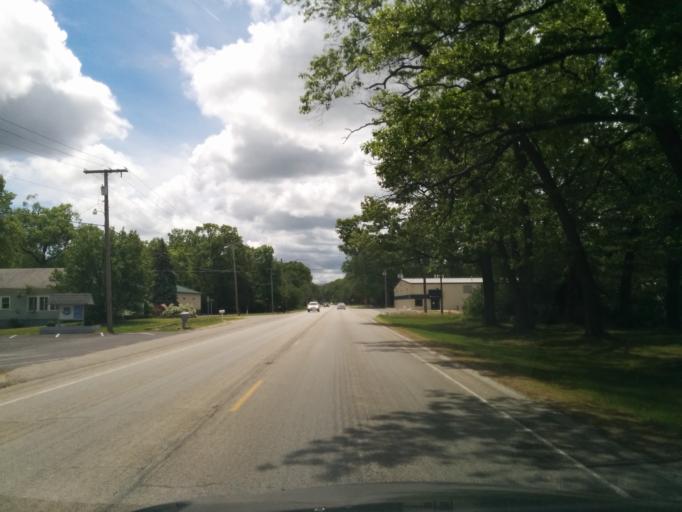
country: US
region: Indiana
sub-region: LaPorte County
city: Michigan City
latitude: 41.6887
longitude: -86.9482
